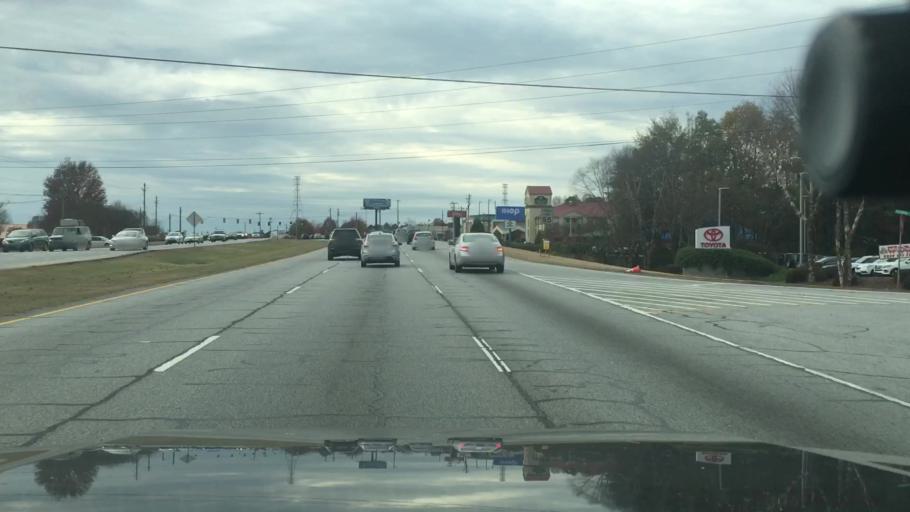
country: US
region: Georgia
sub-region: Coweta County
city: Newnan
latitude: 33.3969
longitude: -84.7555
